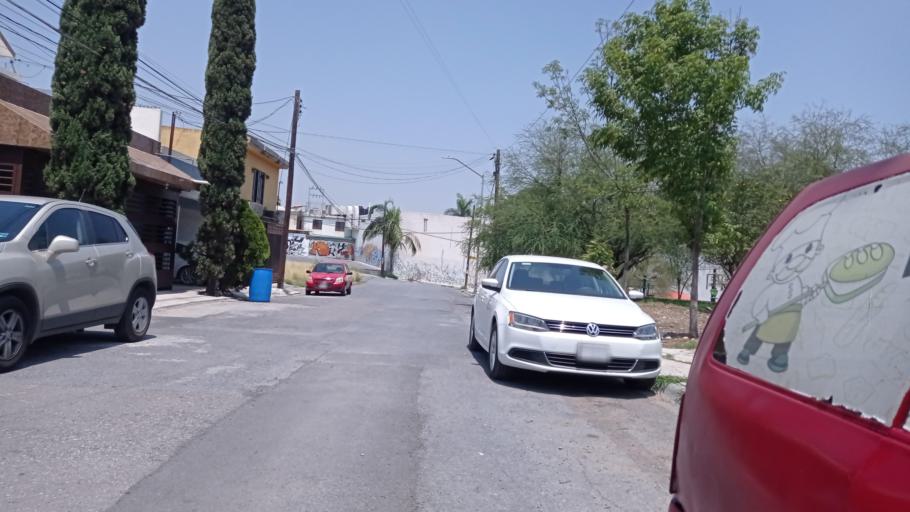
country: MX
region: Nuevo Leon
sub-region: Juarez
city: Jardines de la Silla (Jardines)
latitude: 25.6555
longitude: -100.1900
